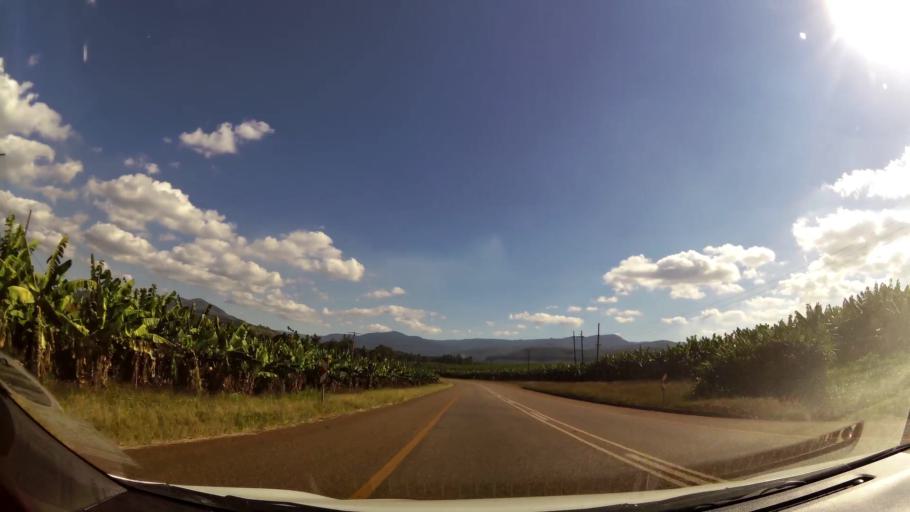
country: ZA
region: Limpopo
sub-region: Mopani District Municipality
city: Tzaneen
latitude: -23.8031
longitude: 30.1176
